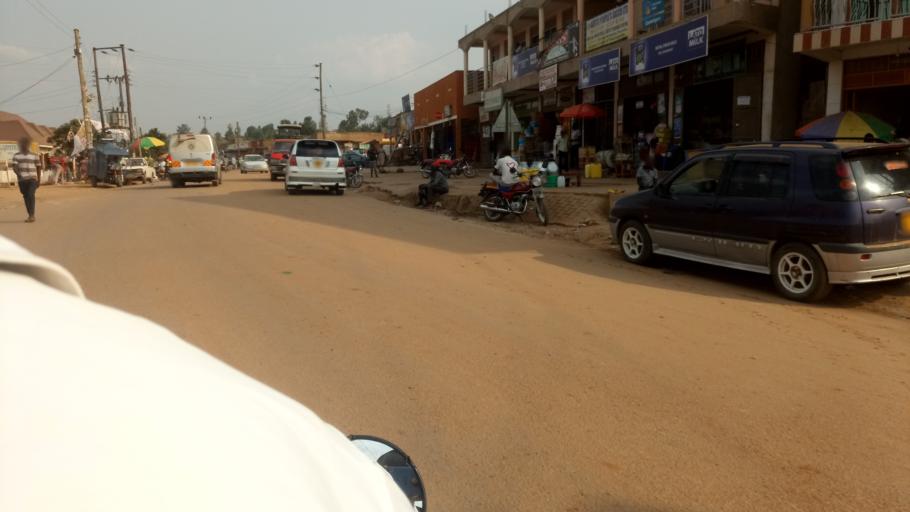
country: UG
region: Western Region
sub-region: Mbarara District
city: Mbarara
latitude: -0.6186
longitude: 30.6694
